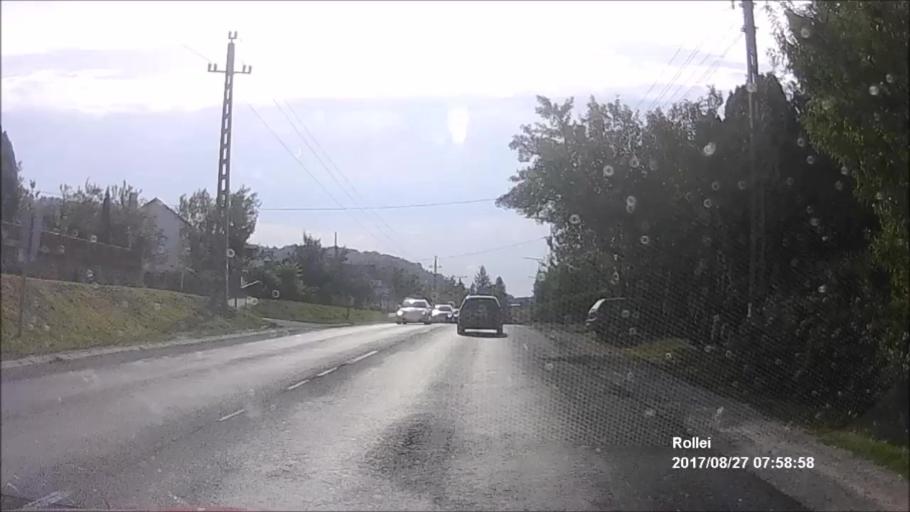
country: HU
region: Zala
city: Gyenesdias
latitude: 46.7715
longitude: 17.2910
